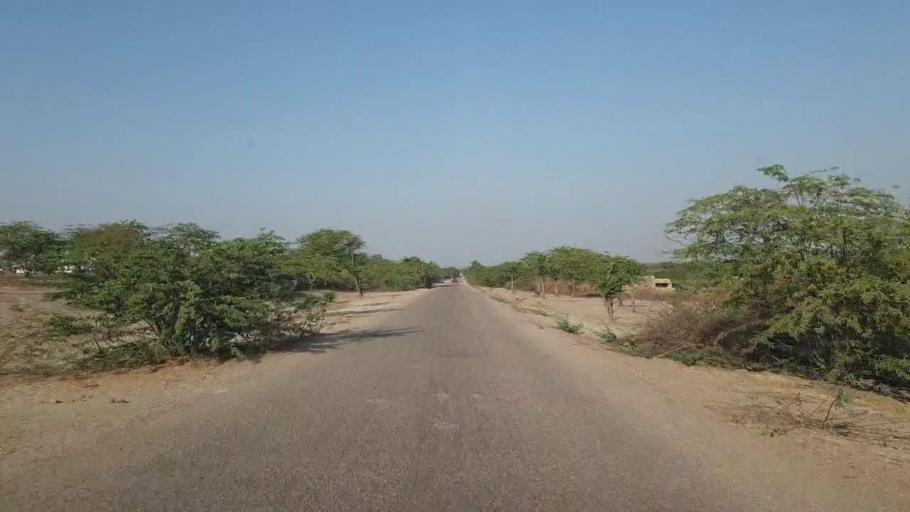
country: PK
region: Sindh
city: Chor
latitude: 25.5446
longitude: 69.7826
